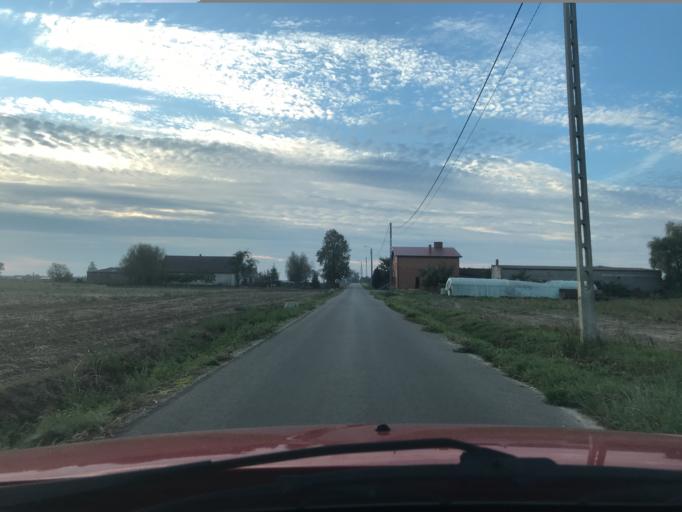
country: PL
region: Greater Poland Voivodeship
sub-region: Powiat ostrowski
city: Skalmierzyce
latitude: 51.7613
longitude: 17.8986
